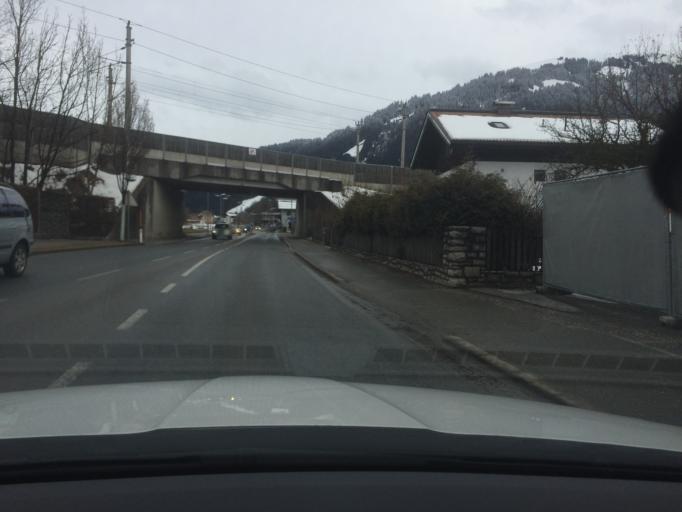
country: AT
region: Tyrol
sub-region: Politischer Bezirk Kitzbuhel
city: Kitzbuhel
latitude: 47.4427
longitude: 12.3991
